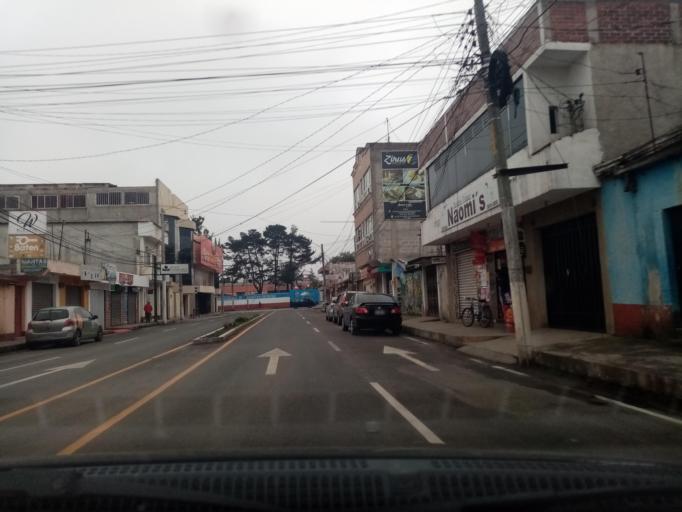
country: GT
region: Quetzaltenango
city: Quetzaltenango
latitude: 14.8463
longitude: -91.5219
